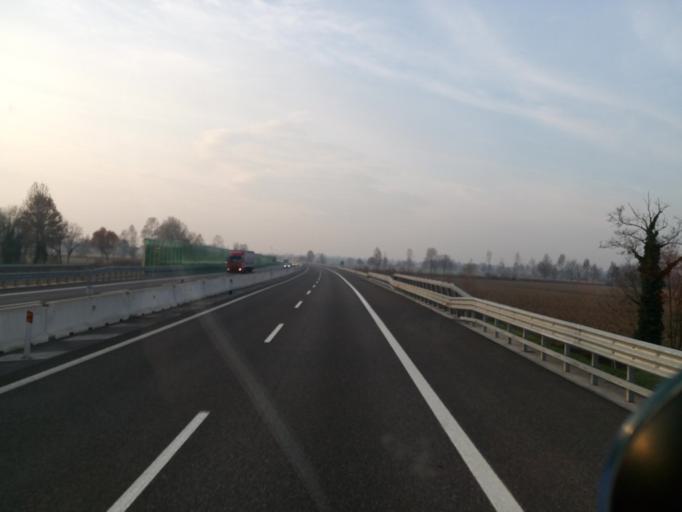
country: IT
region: Lombardy
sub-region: Provincia di Brescia
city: Poncarale
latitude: 45.4724
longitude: 10.1952
